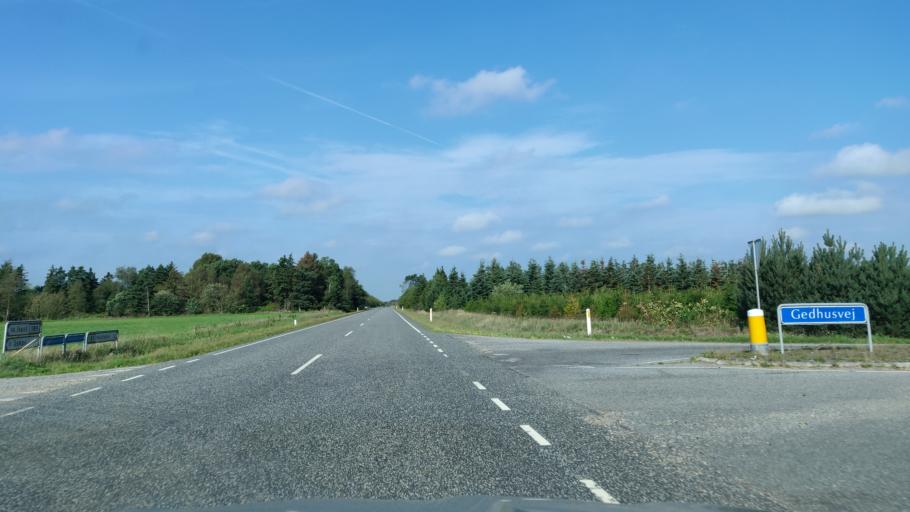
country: DK
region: Central Jutland
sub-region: Herning Kommune
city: Sunds
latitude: 56.2447
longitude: 9.0785
